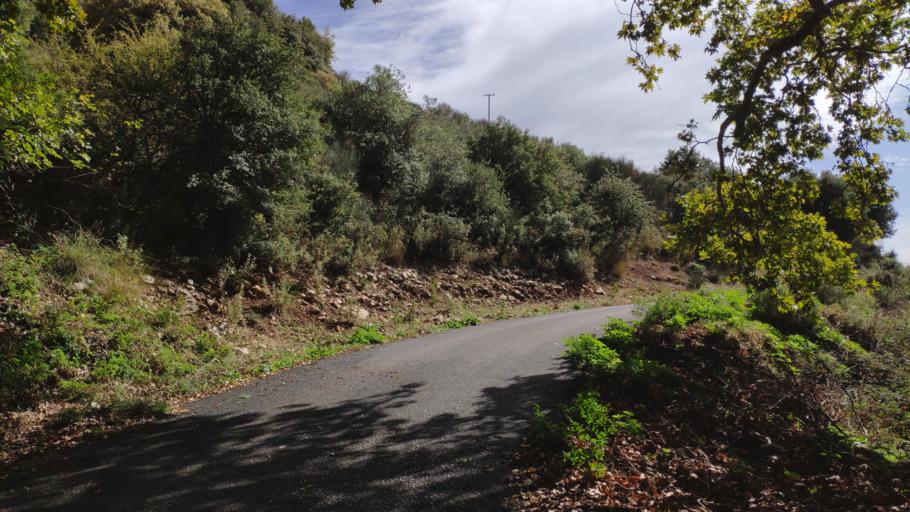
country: GR
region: Peloponnese
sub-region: Nomos Arkadias
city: Dimitsana
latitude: 37.5828
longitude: 22.0477
